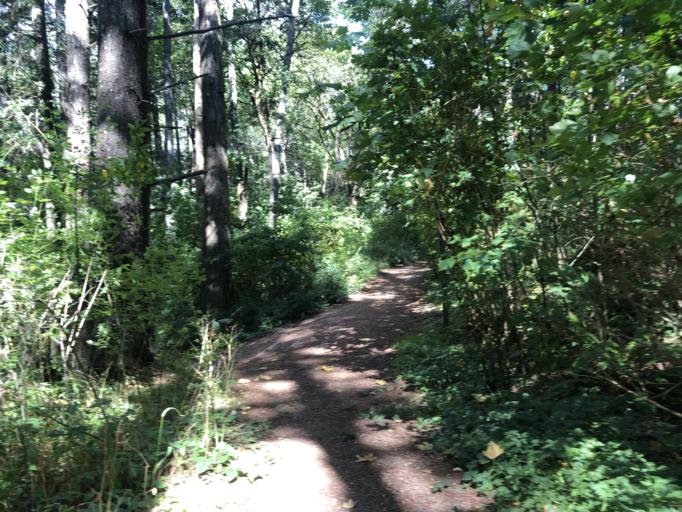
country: CA
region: British Columbia
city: Metchosin
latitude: 48.3643
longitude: -123.5388
